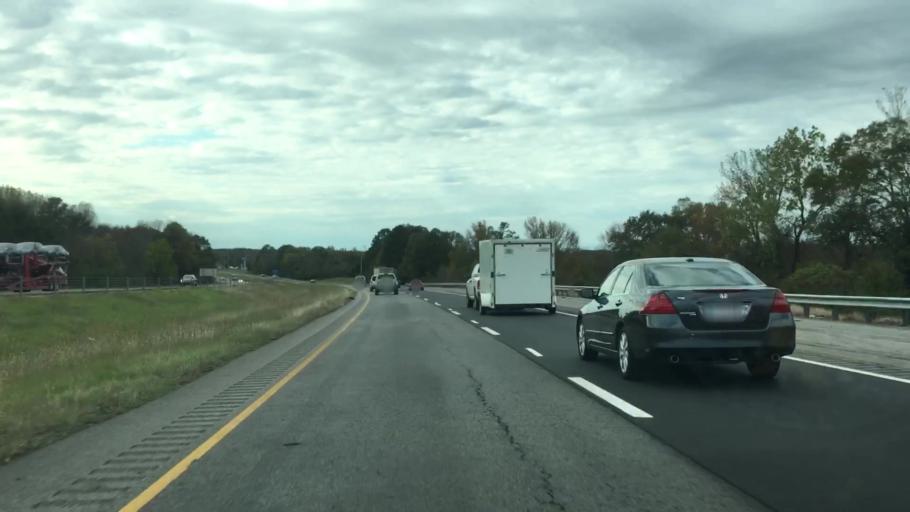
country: US
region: Arkansas
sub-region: Conway County
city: Morrilton
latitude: 35.1731
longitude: -92.7012
